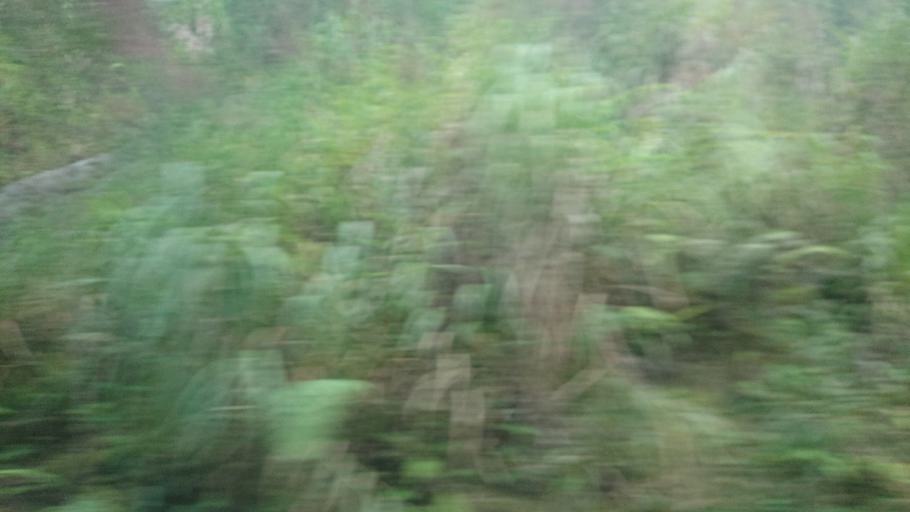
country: TW
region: Taiwan
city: Lugu
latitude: 23.5063
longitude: 120.7898
